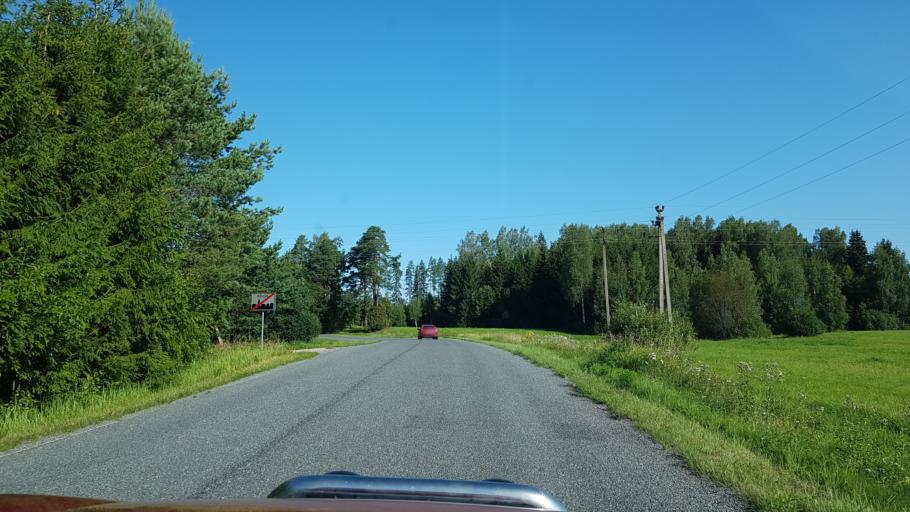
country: EE
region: Vorumaa
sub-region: Voru linn
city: Voru
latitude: 57.7355
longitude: 26.9273
